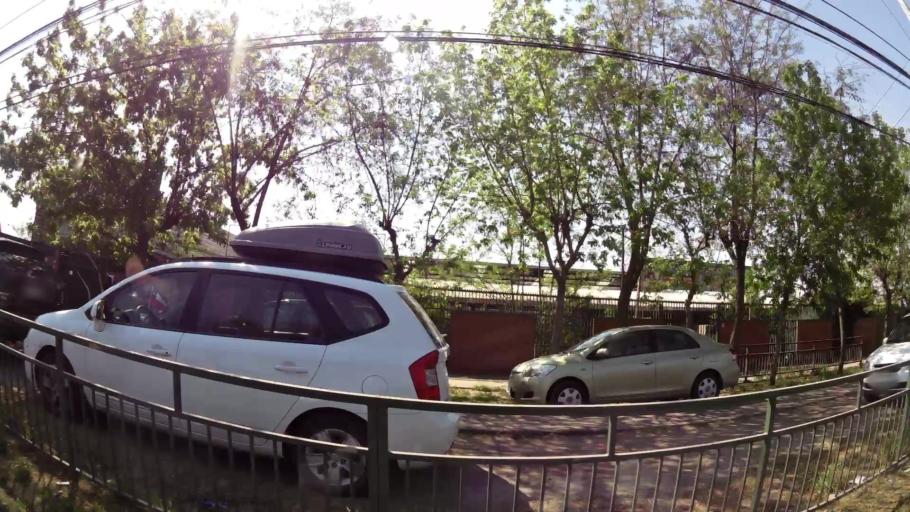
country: CL
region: Santiago Metropolitan
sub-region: Provincia de Santiago
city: La Pintana
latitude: -33.5467
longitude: -70.6071
